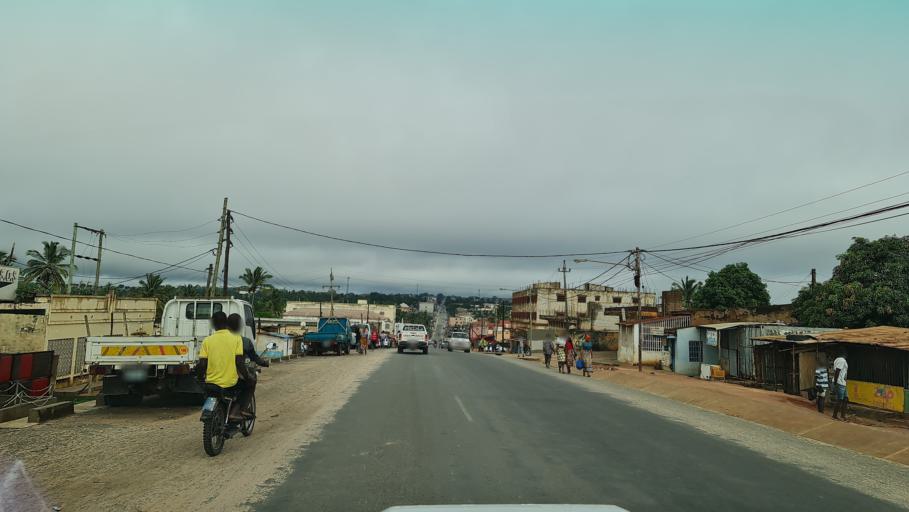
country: MZ
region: Nampula
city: Nampula
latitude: -15.1339
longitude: 39.2748
